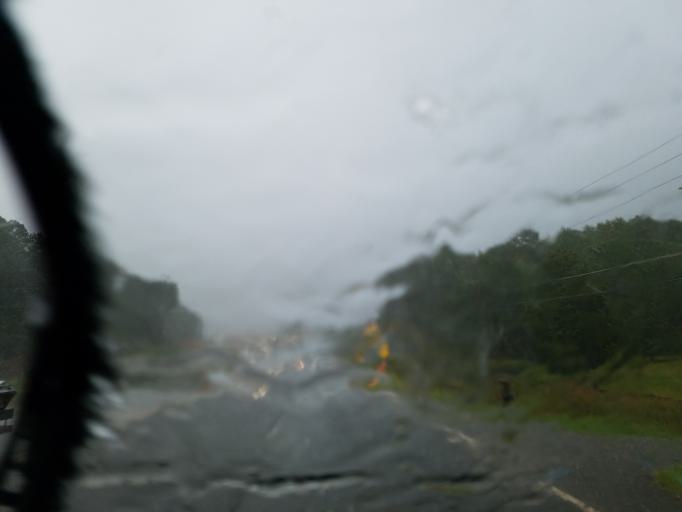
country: US
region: Georgia
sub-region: Bartow County
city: Adairsville
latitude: 34.3694
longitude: -84.9962
